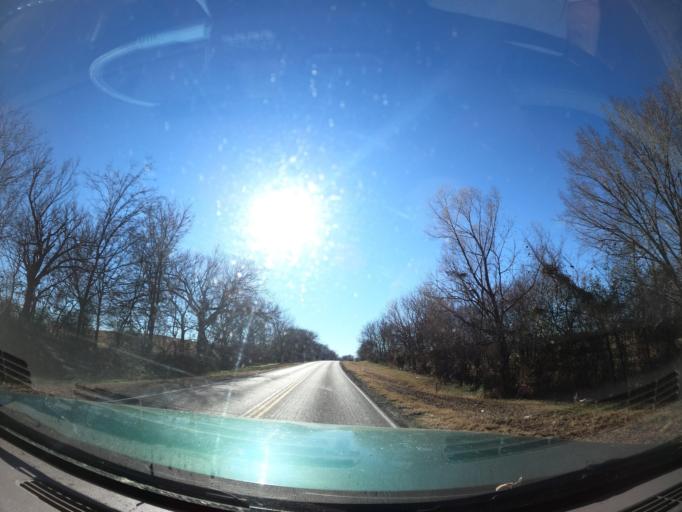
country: US
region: Oklahoma
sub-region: Muskogee County
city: Haskell
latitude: 35.6628
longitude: -95.6459
